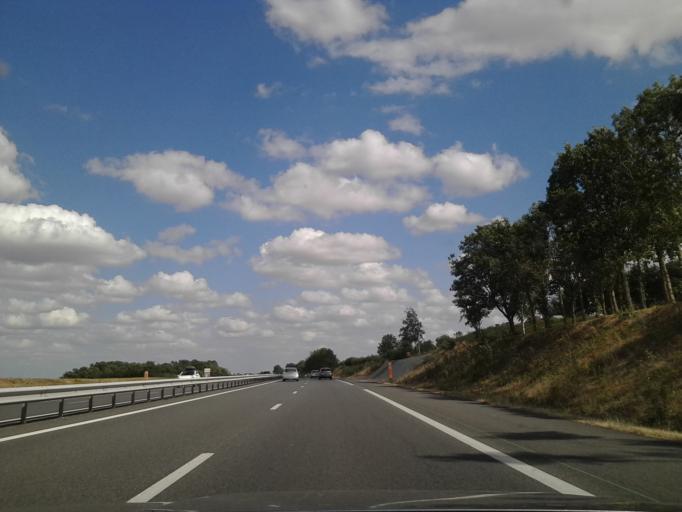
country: FR
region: Auvergne
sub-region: Departement de l'Allier
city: Vallon-en-Sully
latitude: 46.5166
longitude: 2.5811
